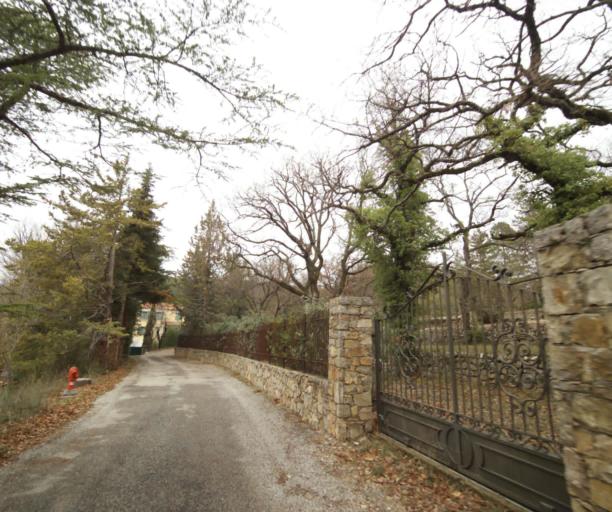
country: FR
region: Provence-Alpes-Cote d'Azur
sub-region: Departement du Var
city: Trans-en-Provence
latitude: 43.5149
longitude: 6.4804
